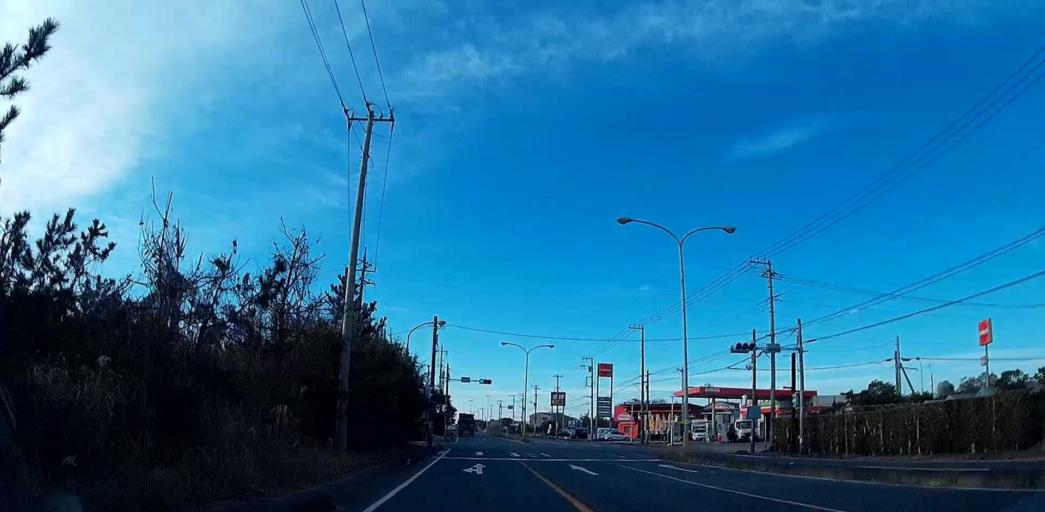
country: JP
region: Chiba
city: Omigawa
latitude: 35.8218
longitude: 140.7306
